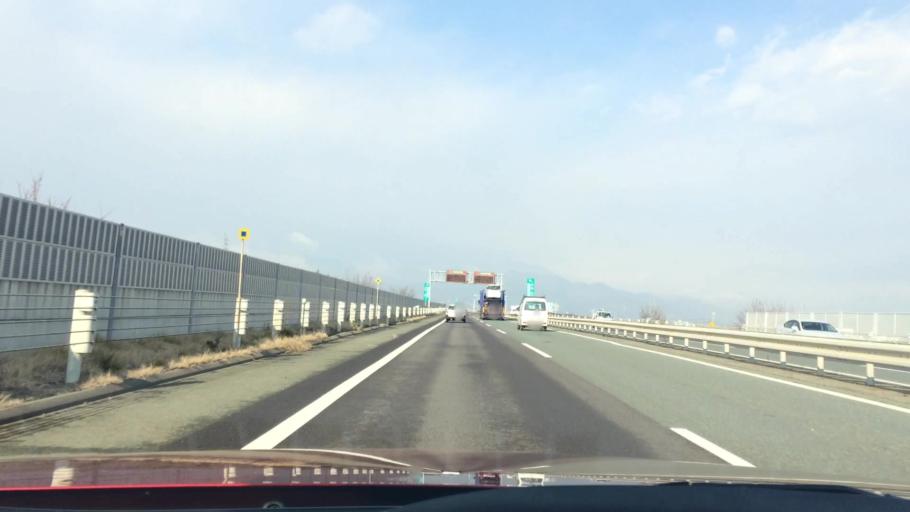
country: JP
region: Nagano
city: Nagano-shi
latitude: 36.5426
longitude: 138.1394
